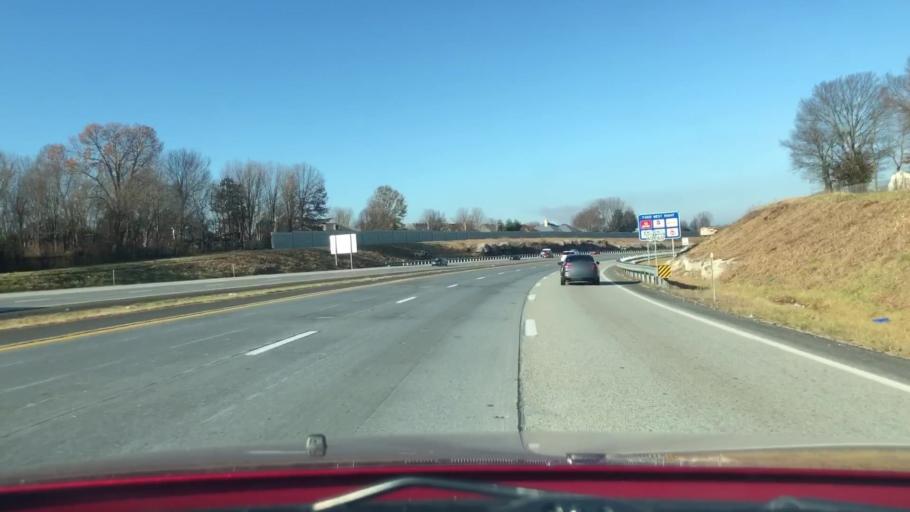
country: US
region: Missouri
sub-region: Greene County
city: Battlefield
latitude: 37.1350
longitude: -93.3041
